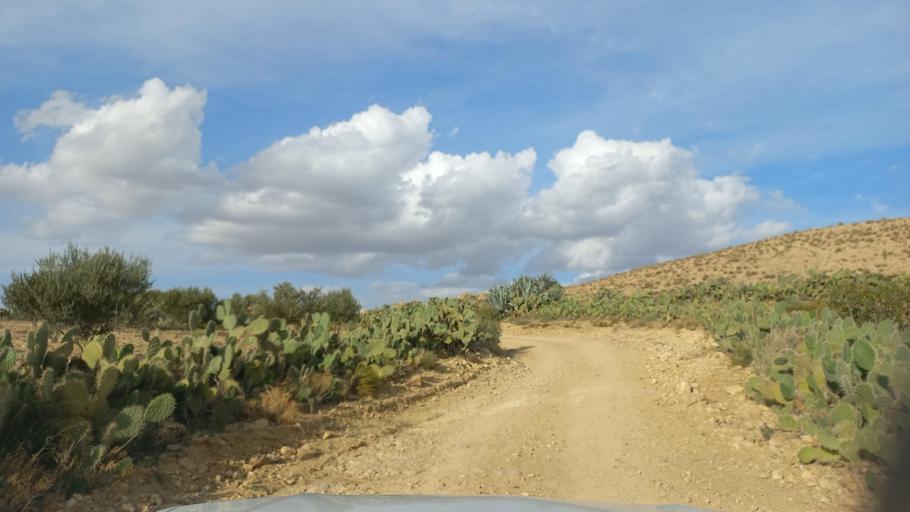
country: TN
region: Al Qasrayn
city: Sbiba
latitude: 35.4581
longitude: 9.0823
